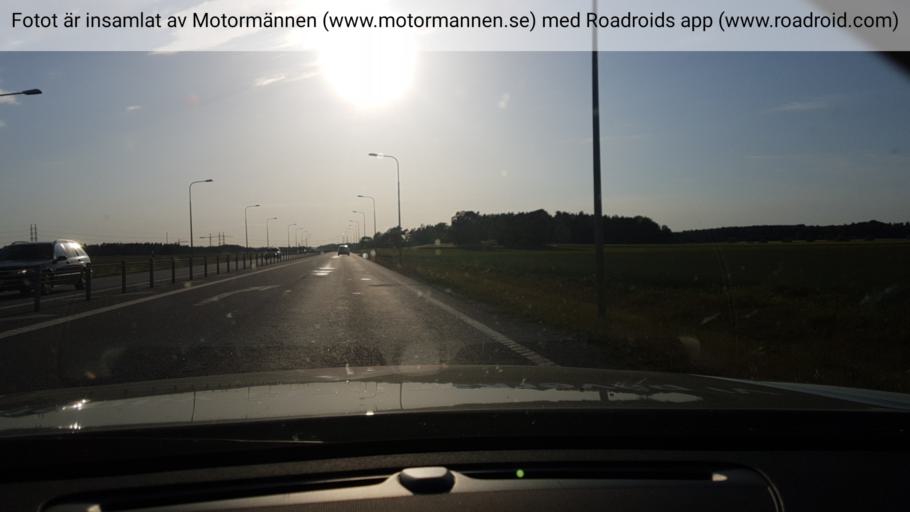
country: SE
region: Uppsala
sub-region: Uppsala Kommun
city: Gamla Uppsala
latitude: 59.8884
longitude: 17.6876
